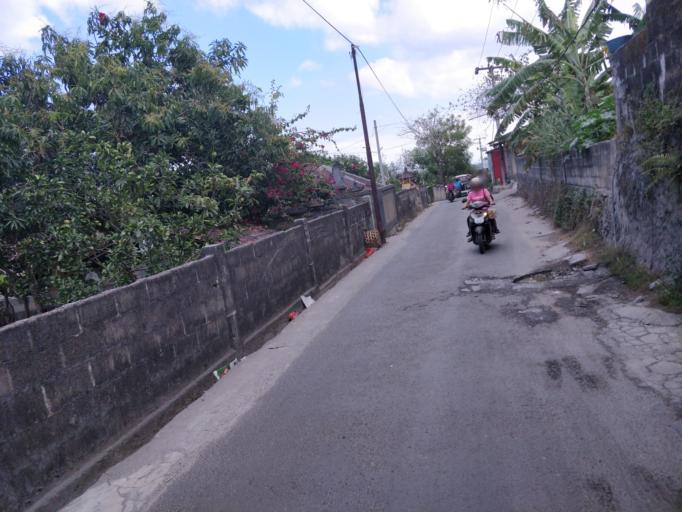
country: ID
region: Bali
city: Lembongan Kawan
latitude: -8.6888
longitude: 115.4389
